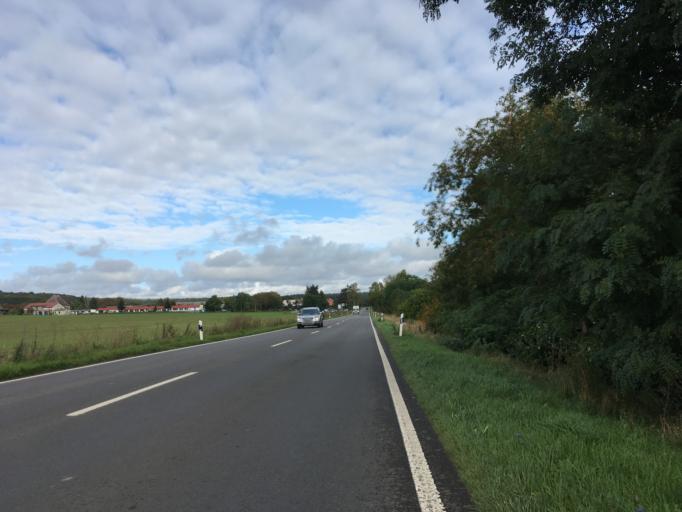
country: DE
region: Brandenburg
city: Oderberg
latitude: 52.8876
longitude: 14.0574
